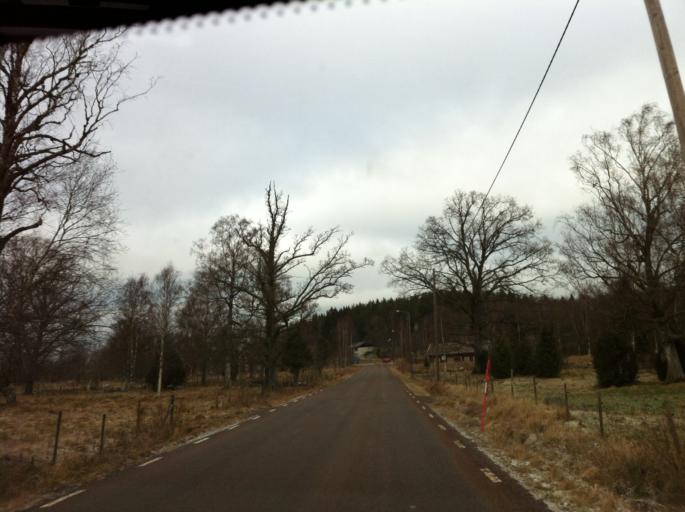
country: SE
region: Joenkoeping
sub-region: Eksjo Kommun
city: Mariannelund
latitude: 57.6305
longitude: 15.7123
